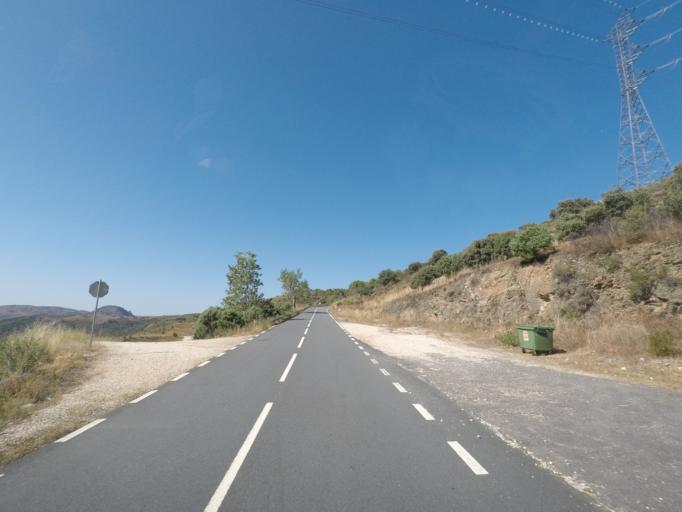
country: ES
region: Castille and Leon
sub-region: Provincia de Salamanca
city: Villarino de los Aires
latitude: 41.3028
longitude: -6.4817
